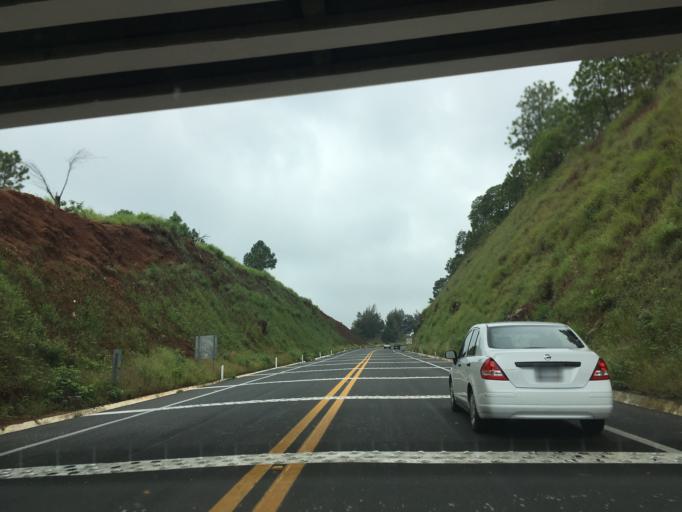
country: MX
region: Michoacan
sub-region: Ziracuaretiro
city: Patuan
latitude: 19.4168
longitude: -101.9603
